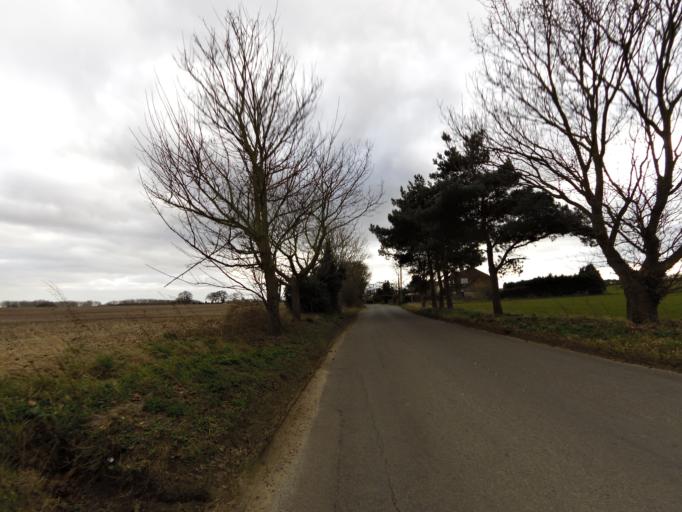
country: GB
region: England
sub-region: Suffolk
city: Shotley Gate
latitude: 52.0229
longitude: 1.2995
